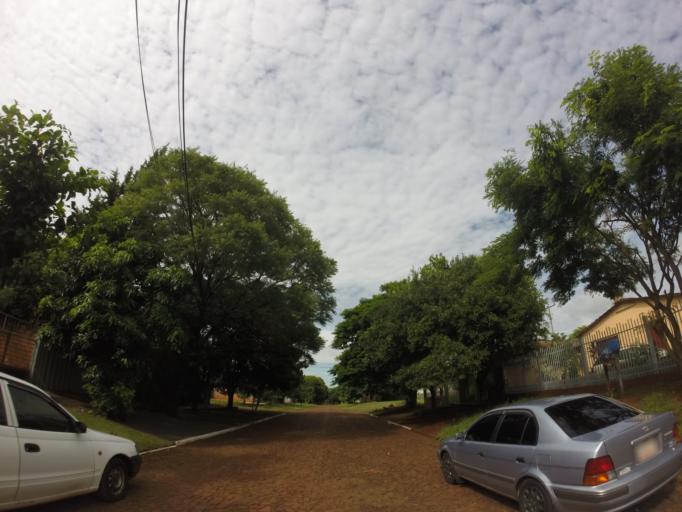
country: PY
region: Alto Parana
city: Ciudad del Este
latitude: -25.4085
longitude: -54.6446
